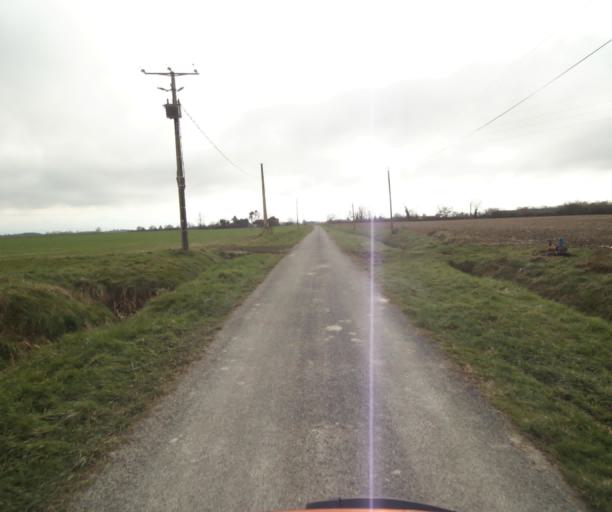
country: FR
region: Midi-Pyrenees
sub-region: Departement de l'Ariege
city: Mazeres
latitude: 43.2038
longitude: 1.6800
